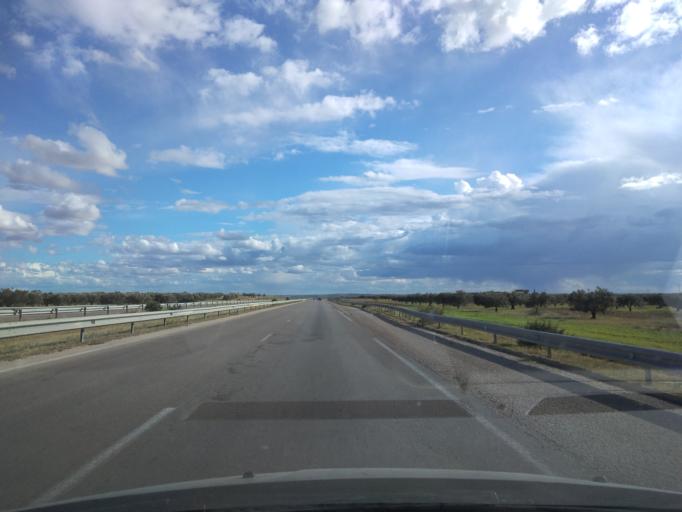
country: TN
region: Al Munastir
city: Manzil Kamil
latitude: 35.6159
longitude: 10.5957
